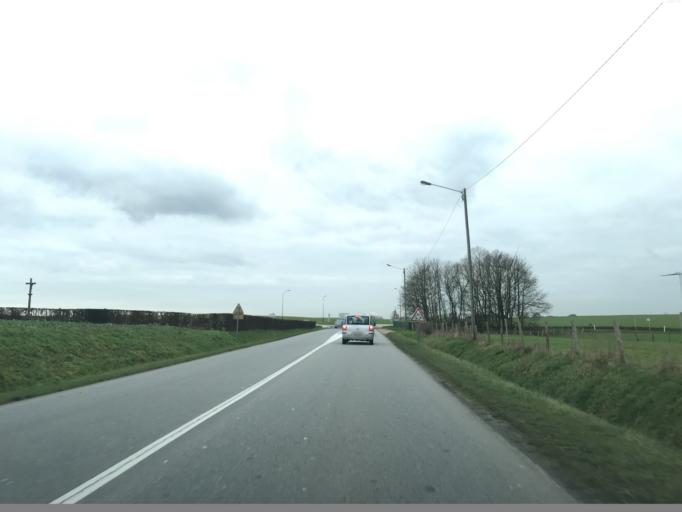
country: FR
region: Haute-Normandie
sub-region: Departement de l'Eure
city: Pont-Saint-Pierre
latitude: 49.3876
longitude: 1.3016
